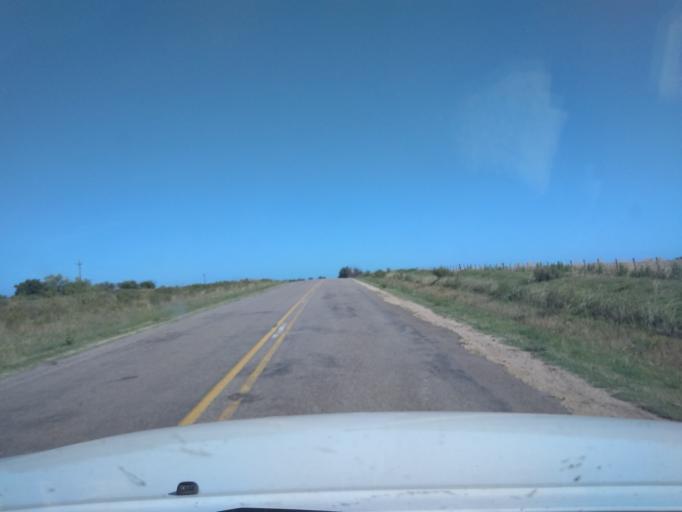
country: UY
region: Canelones
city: San Ramon
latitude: -34.2090
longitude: -55.9303
